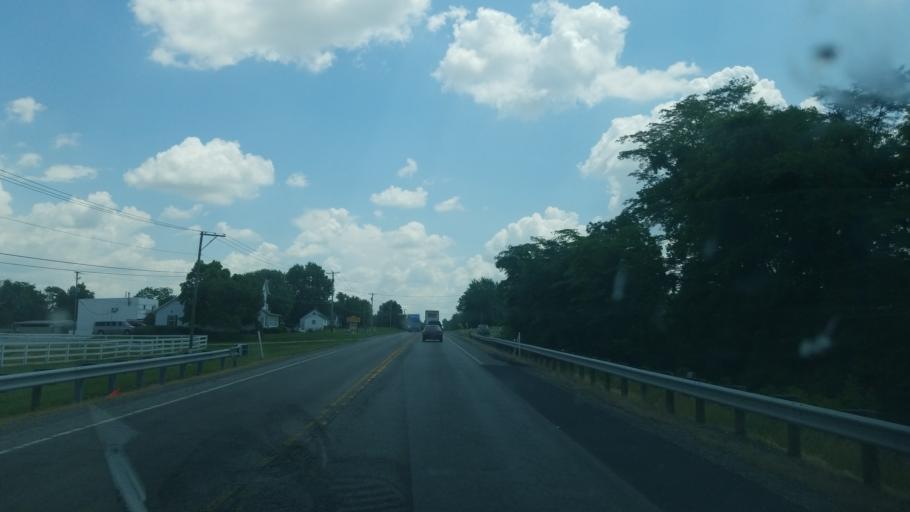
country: US
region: Ohio
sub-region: Allen County
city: Lima
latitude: 40.7310
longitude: -84.0402
